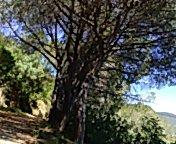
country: IT
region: Tuscany
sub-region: Provincia di Livorno
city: Capoliveri
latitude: 42.7476
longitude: 10.3192
